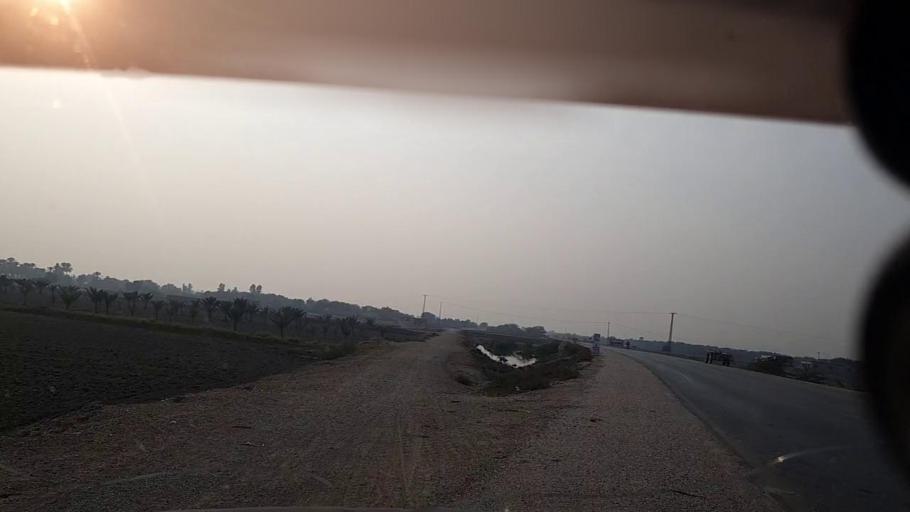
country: PK
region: Sindh
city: Gambat
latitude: 27.4358
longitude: 68.6130
